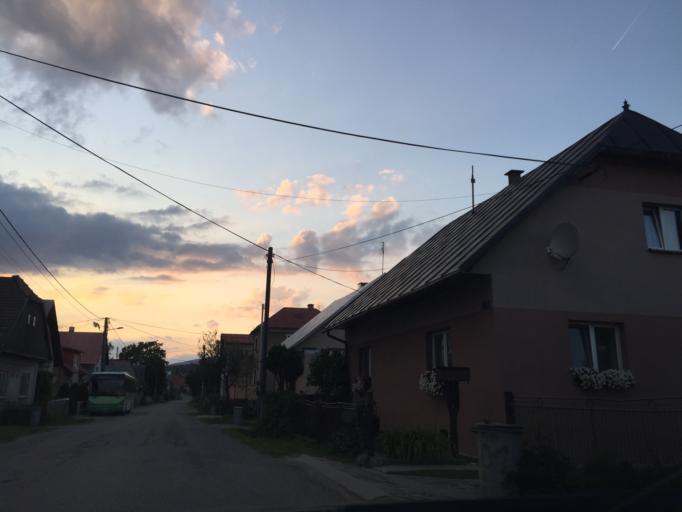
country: PL
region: Silesian Voivodeship
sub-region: Powiat zywiecki
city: Sopotnia Wielka
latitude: 49.4653
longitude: 19.3143
